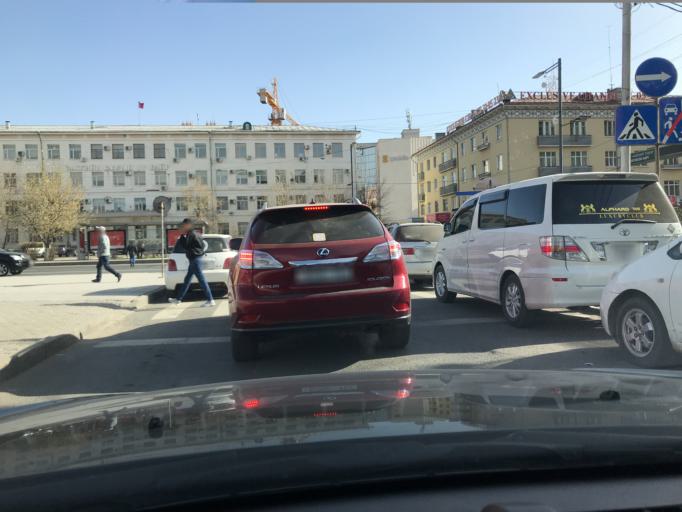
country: MN
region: Ulaanbaatar
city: Ulaanbaatar
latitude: 47.9182
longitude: 106.9113
